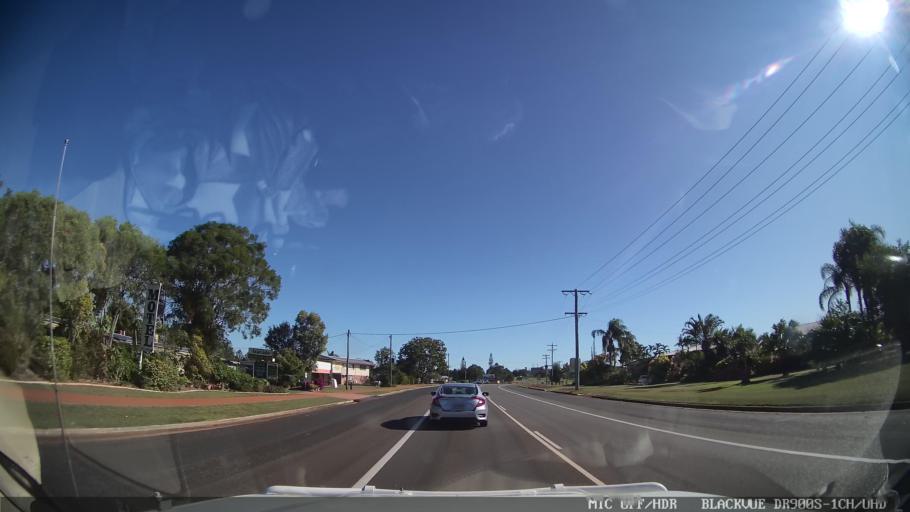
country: AU
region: Queensland
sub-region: Bundaberg
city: Childers
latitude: -25.2335
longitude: 152.2692
